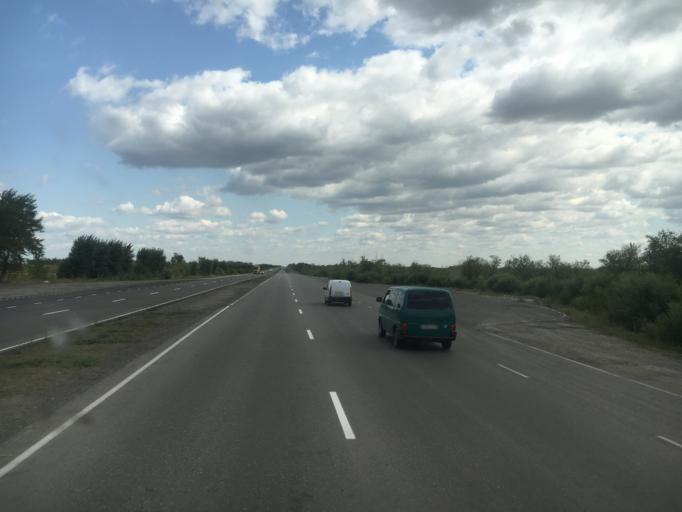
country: KZ
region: Qostanay
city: Rudnyy
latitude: 52.9902
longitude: 63.2494
